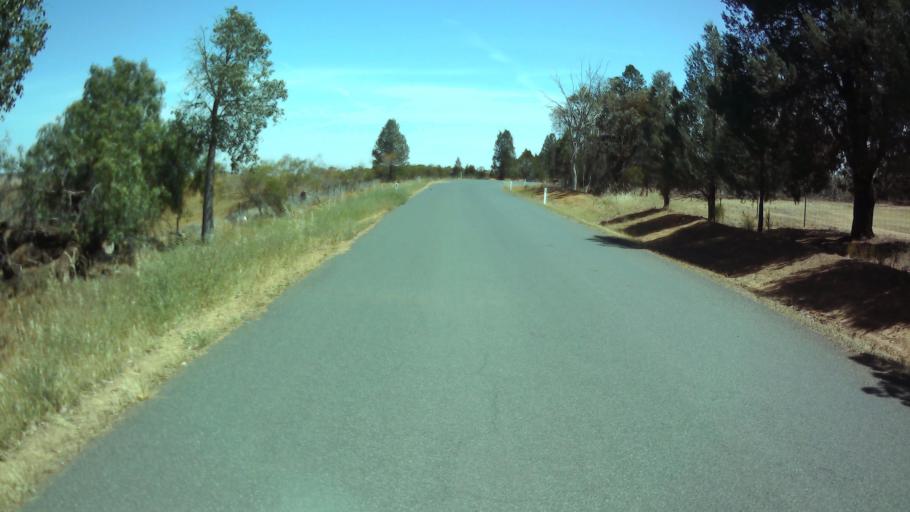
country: AU
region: New South Wales
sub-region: Weddin
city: Grenfell
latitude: -33.9052
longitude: 148.1825
